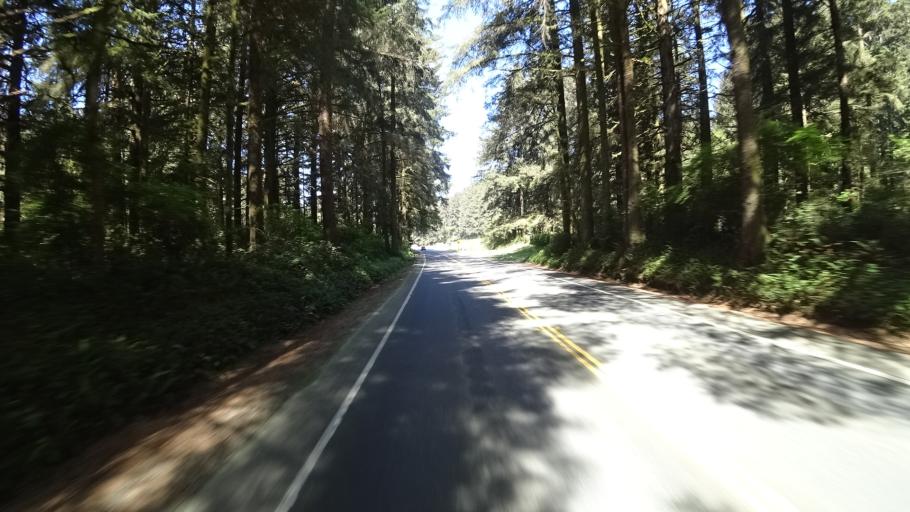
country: US
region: California
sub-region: Del Norte County
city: Bertsch-Oceanview
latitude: 41.5833
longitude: -124.0836
